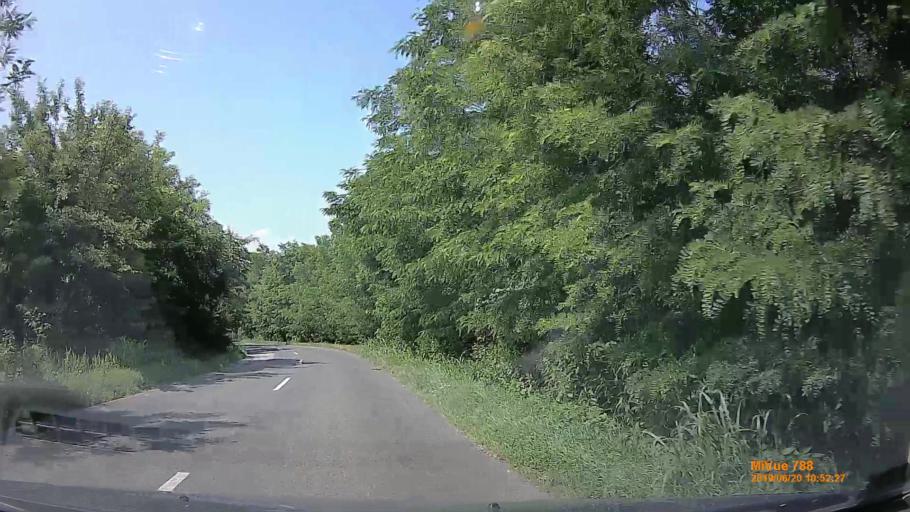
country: HU
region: Baranya
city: Mecseknadasd
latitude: 46.1567
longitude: 18.5794
